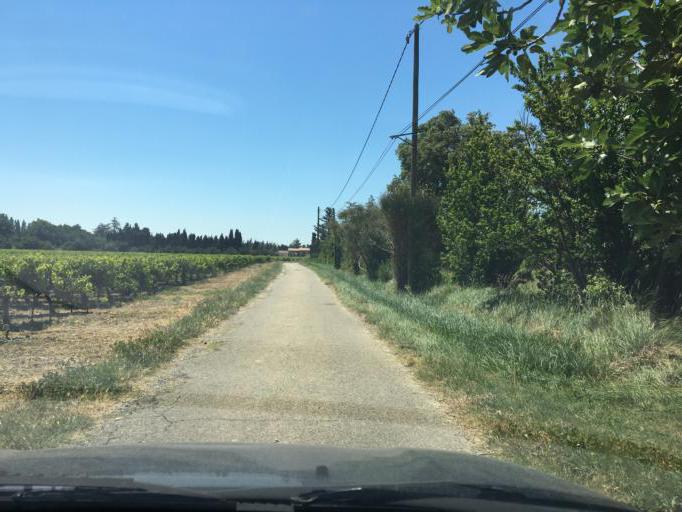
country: FR
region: Provence-Alpes-Cote d'Azur
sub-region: Departement du Vaucluse
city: Camaret-sur-Aigues
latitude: 44.1773
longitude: 4.8958
